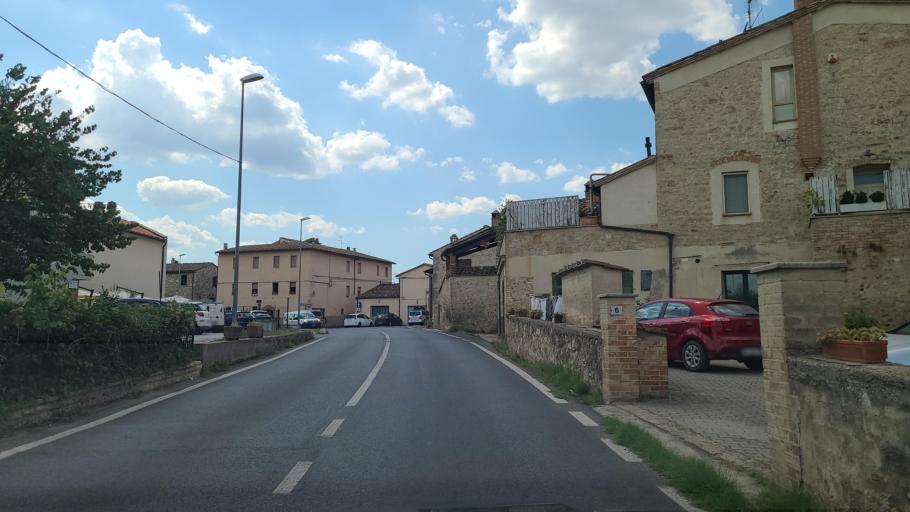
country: IT
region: Tuscany
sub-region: Provincia di Siena
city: Colle di Val d'Elsa
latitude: 43.4150
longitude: 11.0804
